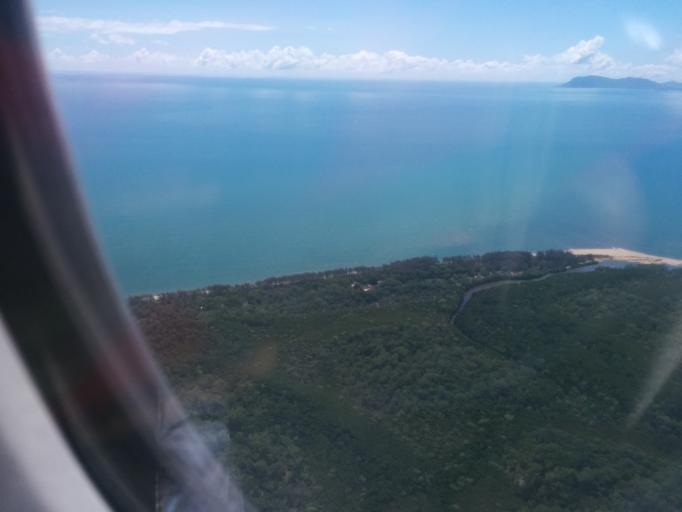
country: AU
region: Queensland
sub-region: Cairns
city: Yorkeys Knob
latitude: -16.8160
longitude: 145.7212
